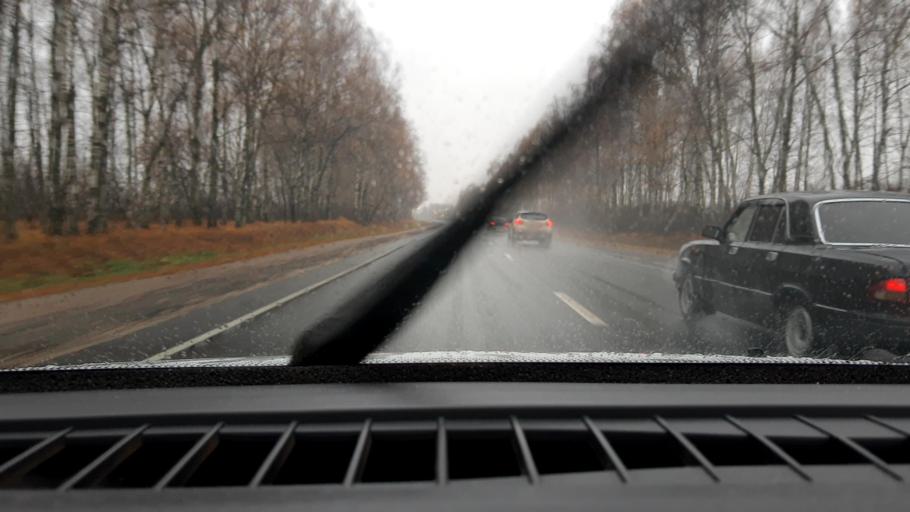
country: RU
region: Nizjnij Novgorod
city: Sitniki
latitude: 56.5128
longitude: 44.0240
